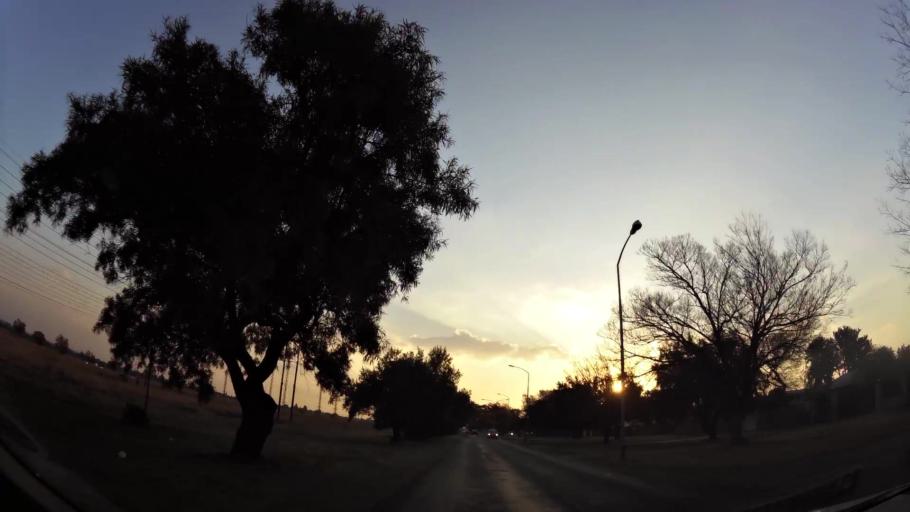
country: ZA
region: Gauteng
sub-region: Ekurhuleni Metropolitan Municipality
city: Springs
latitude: -26.3160
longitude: 28.4501
